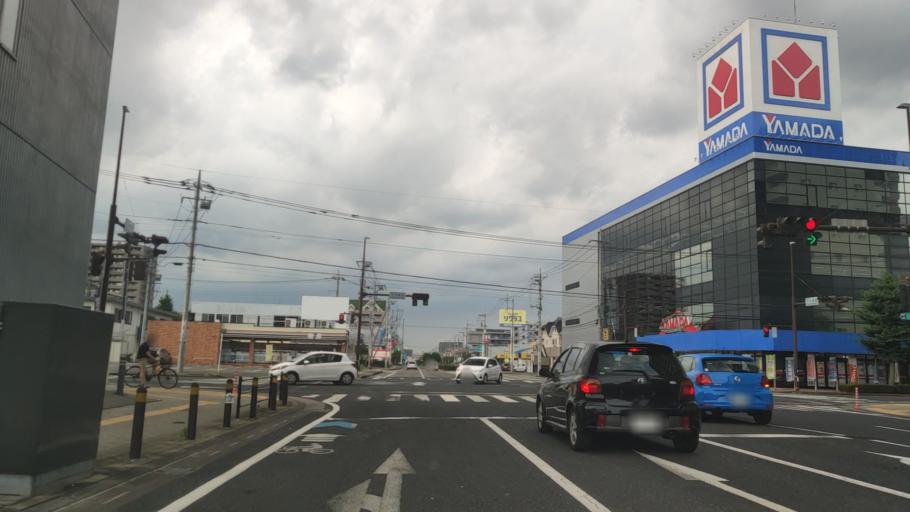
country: JP
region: Tochigi
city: Utsunomiya-shi
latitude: 36.5623
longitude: 139.9042
